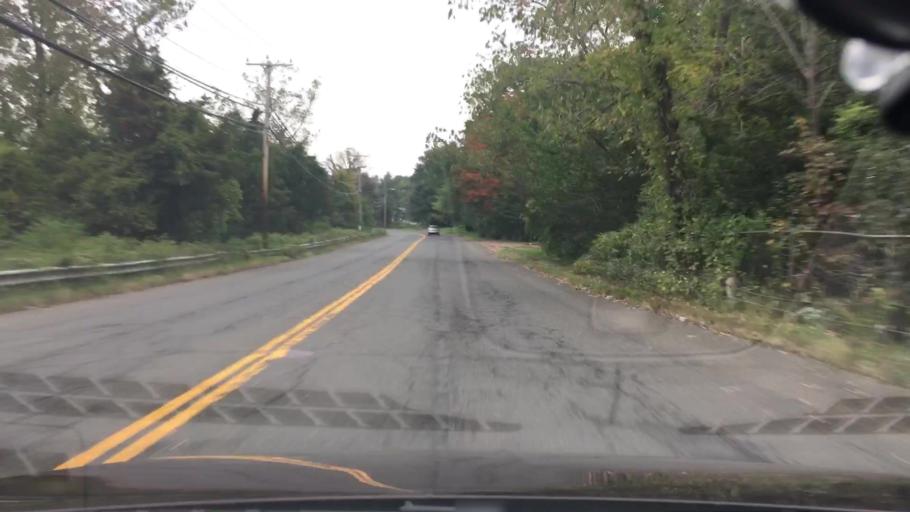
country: US
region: Connecticut
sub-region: Middlesex County
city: Middletown
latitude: 41.5728
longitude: -72.7251
